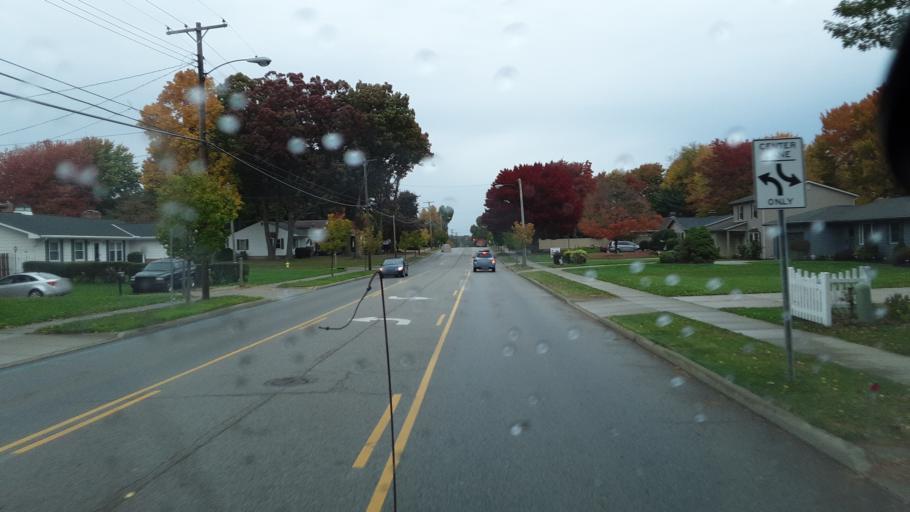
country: US
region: Ohio
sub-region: Summit County
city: Sawyerwood
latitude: 41.0480
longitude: -81.4537
